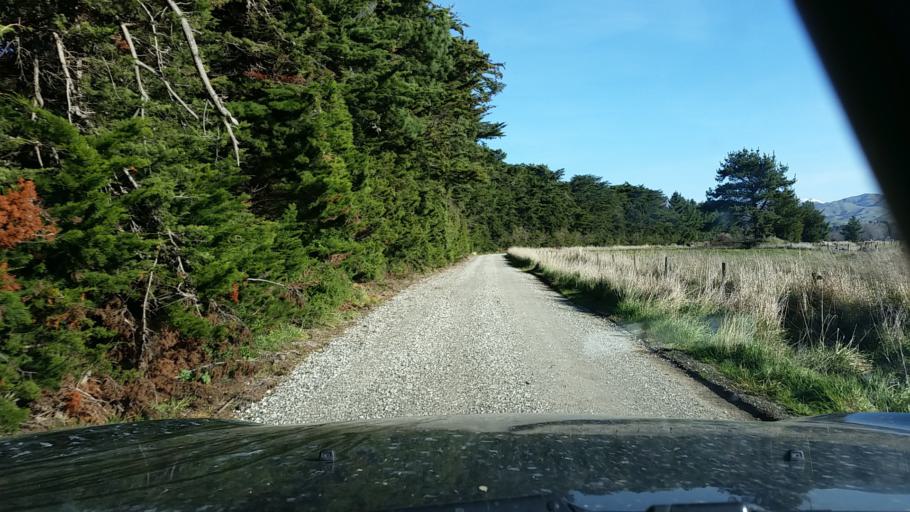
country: NZ
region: Marlborough
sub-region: Marlborough District
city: Blenheim
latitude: -41.8258
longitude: 174.1558
